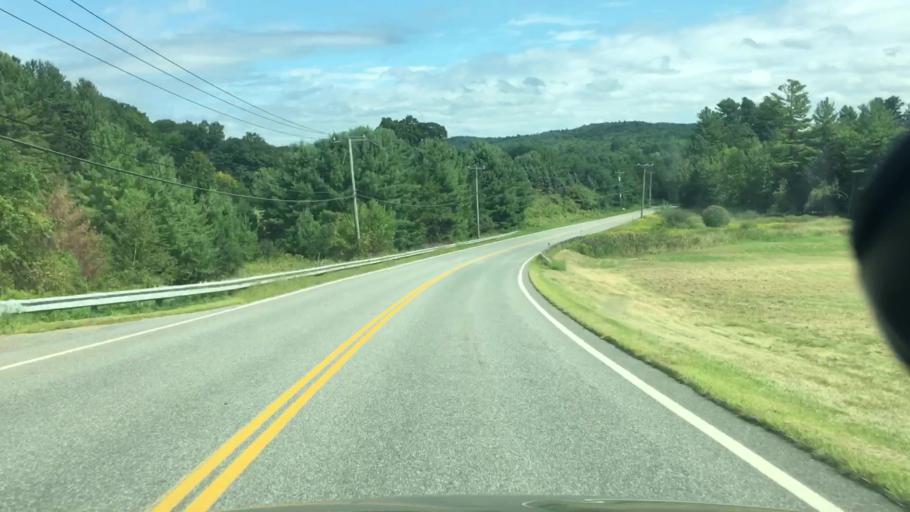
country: US
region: Massachusetts
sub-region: Franklin County
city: Shelburne
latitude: 42.6293
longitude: -72.6695
